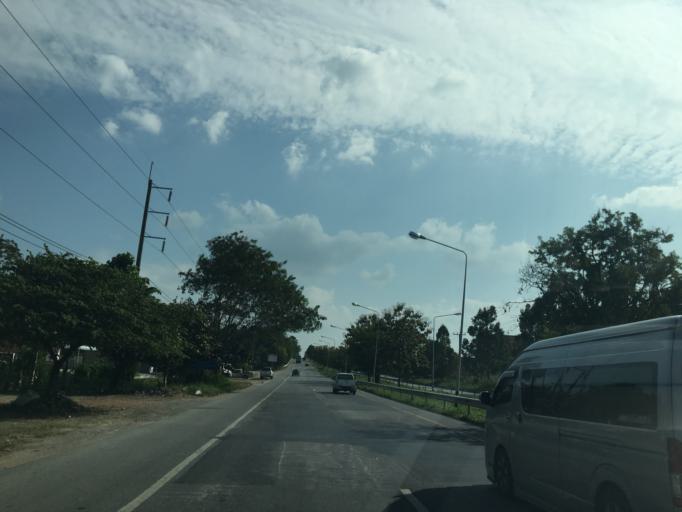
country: TH
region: Chiang Rai
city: Mae Lao
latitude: 19.7011
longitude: 99.7197
